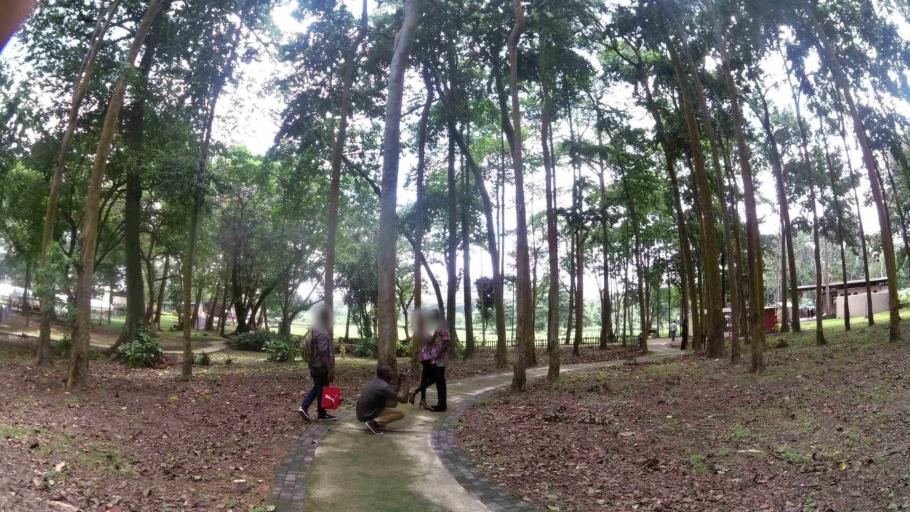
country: NG
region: Oyo
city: Ibadan
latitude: 7.4075
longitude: 3.9023
